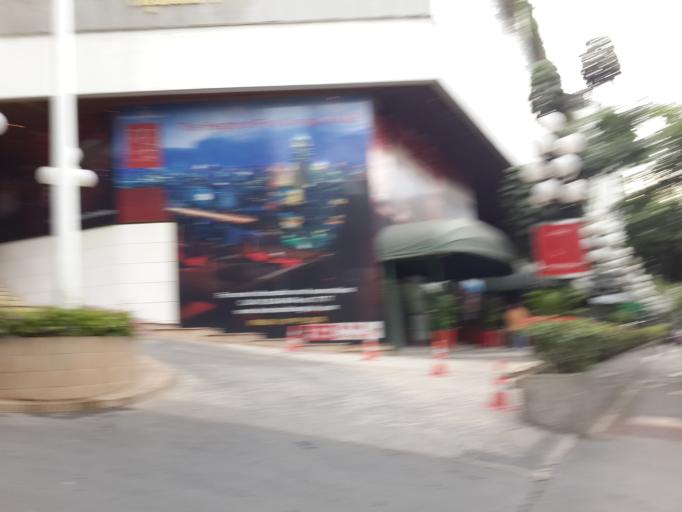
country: TH
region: Bangkok
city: Ratchathewi
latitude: 13.7411
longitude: 100.5541
